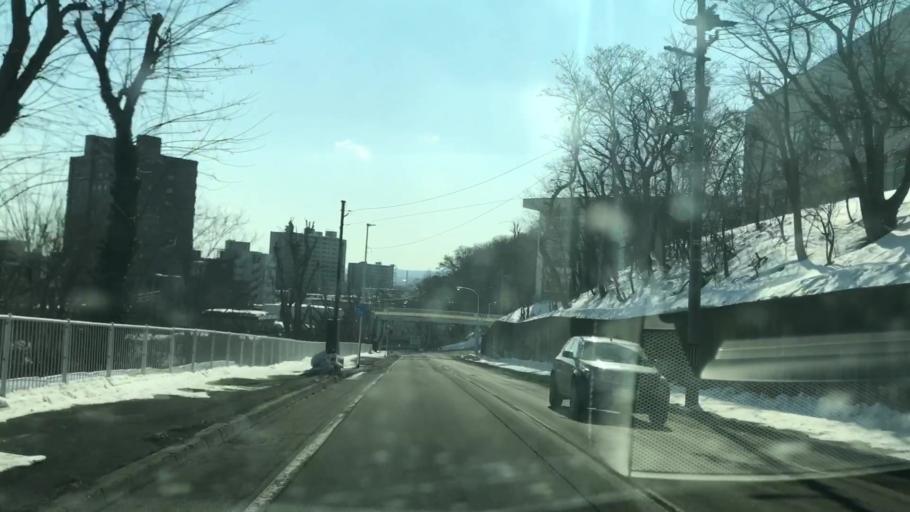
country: JP
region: Hokkaido
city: Sapporo
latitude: 43.0343
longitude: 141.3316
